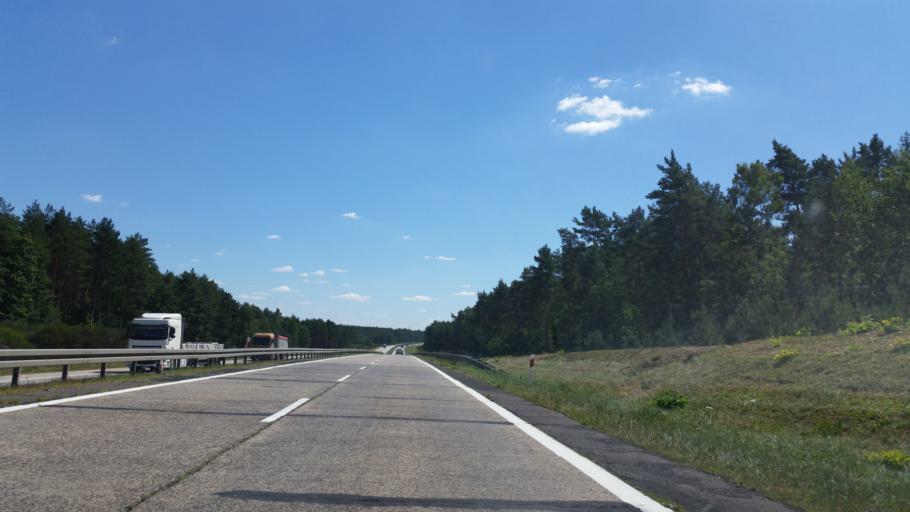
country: PL
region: Lower Silesian Voivodeship
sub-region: Powiat boleslawiecki
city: Boleslawiec
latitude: 51.4042
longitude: 15.5117
